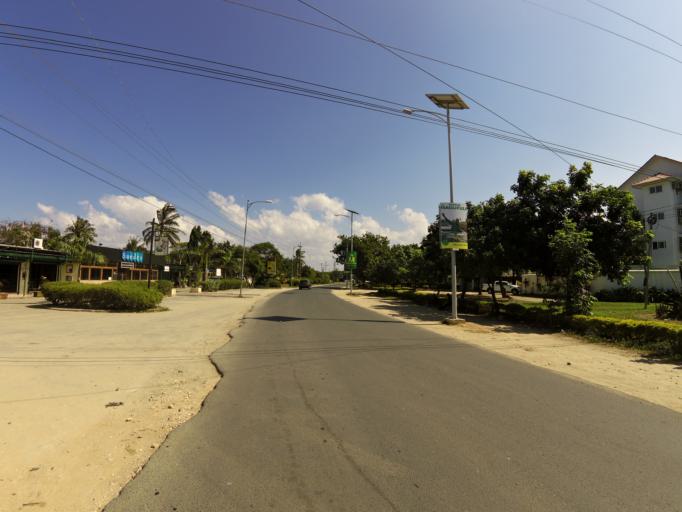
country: TZ
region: Dar es Salaam
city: Magomeni
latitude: -6.7534
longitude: 39.2841
